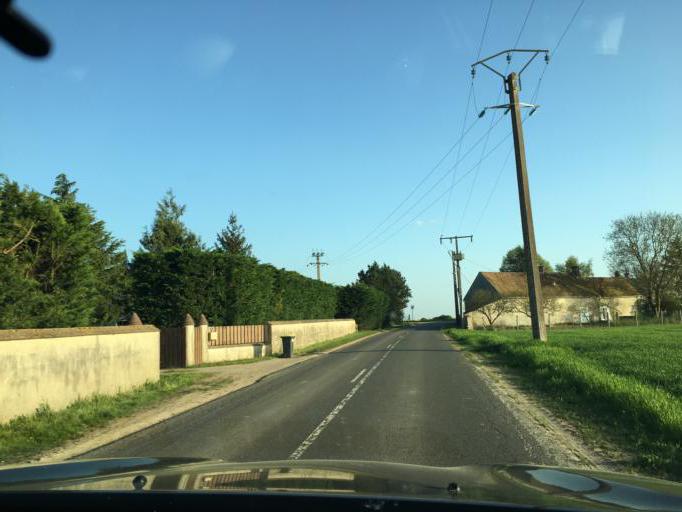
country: FR
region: Centre
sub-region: Departement du Loir-et-Cher
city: Ouzouer-le-Marche
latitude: 47.8821
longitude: 1.5323
